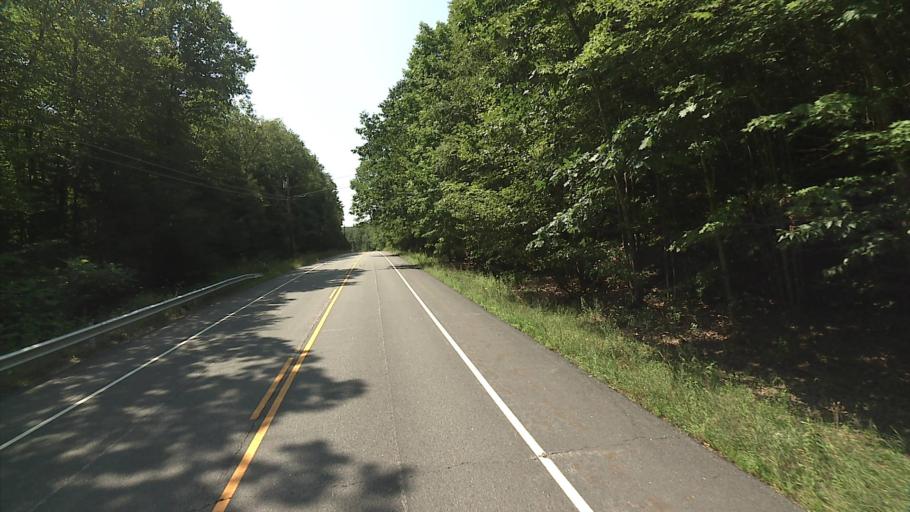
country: US
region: Connecticut
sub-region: Litchfield County
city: Winchester Center
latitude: 41.8724
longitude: -73.1696
